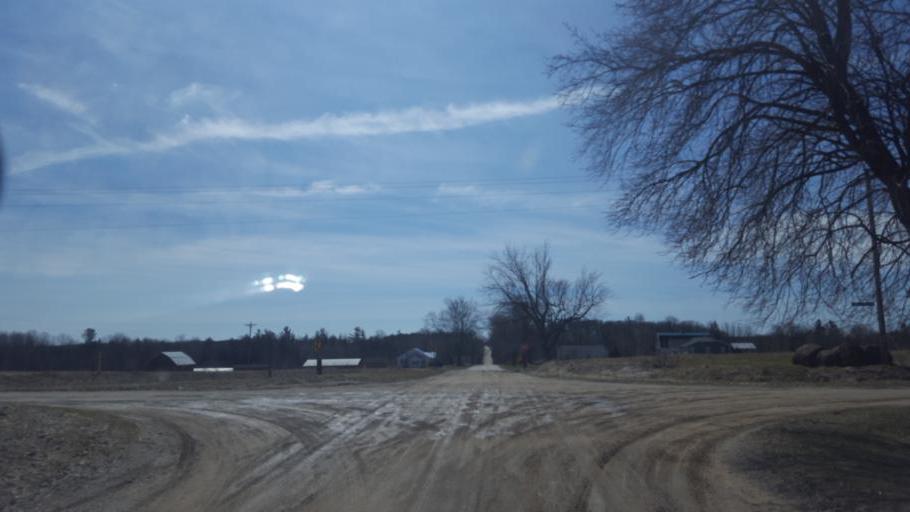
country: US
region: Michigan
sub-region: Montcalm County
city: Edmore
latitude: 43.4880
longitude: -85.0454
